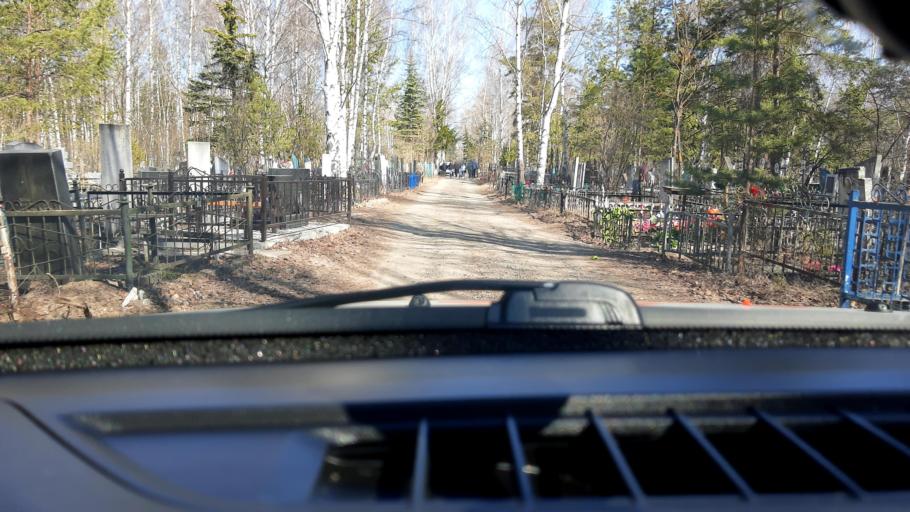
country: RU
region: Nizjnij Novgorod
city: Gorbatovka
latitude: 56.3587
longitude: 43.7855
